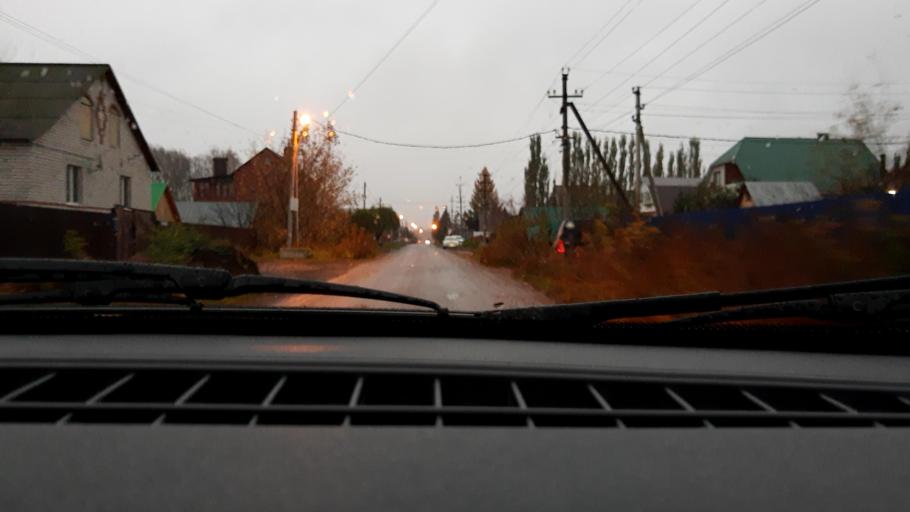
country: RU
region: Bashkortostan
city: Mikhaylovka
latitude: 54.7895
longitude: 55.8975
